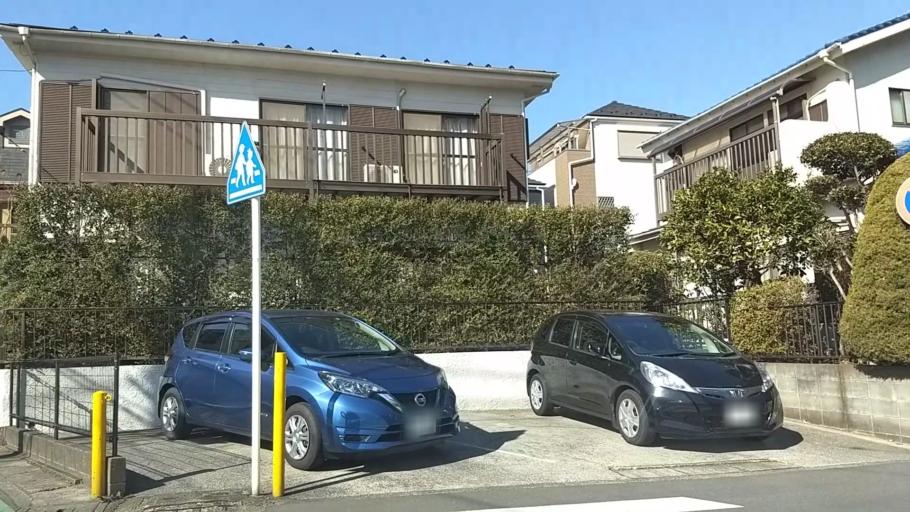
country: JP
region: Kanagawa
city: Yokohama
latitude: 35.5039
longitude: 139.6038
